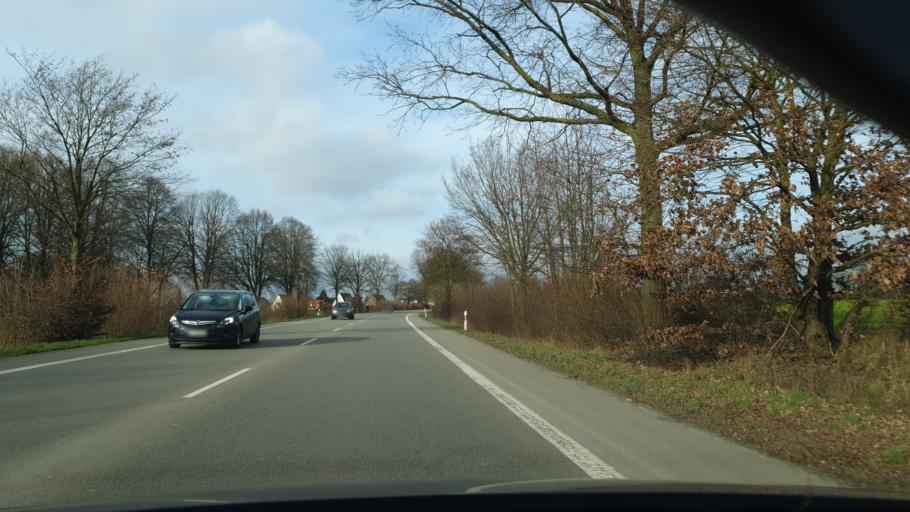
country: DE
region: North Rhine-Westphalia
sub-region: Regierungsbezirk Detmold
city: Bielefeld
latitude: 52.0659
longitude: 8.5178
